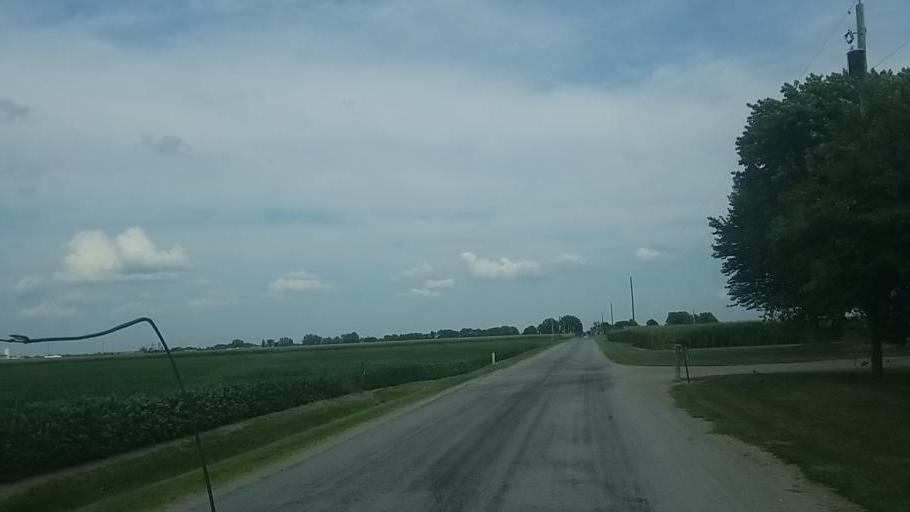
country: US
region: Ohio
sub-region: Wyandot County
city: Upper Sandusky
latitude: 40.8179
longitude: -83.3263
